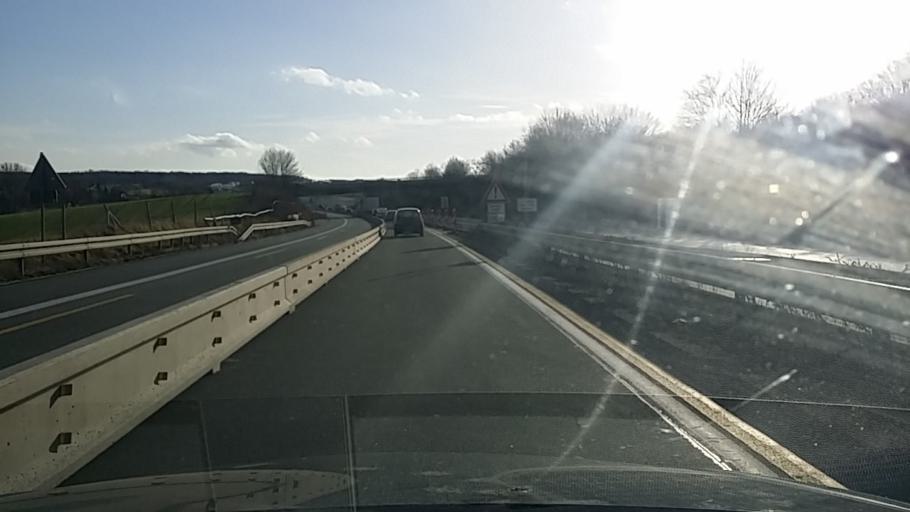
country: DE
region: North Rhine-Westphalia
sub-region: Regierungsbezirk Detmold
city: Paderborn
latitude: 51.6599
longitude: 8.7080
